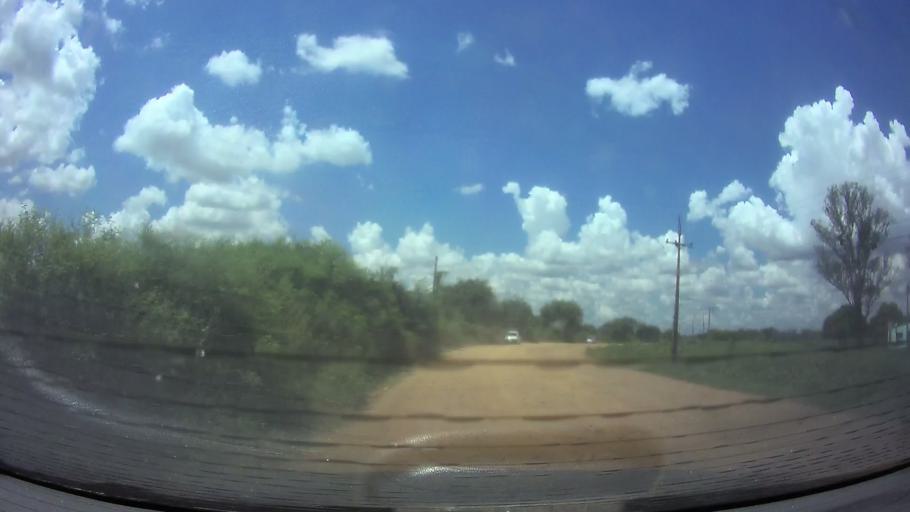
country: PY
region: Presidente Hayes
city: Nanawa
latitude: -25.2448
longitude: -57.6636
